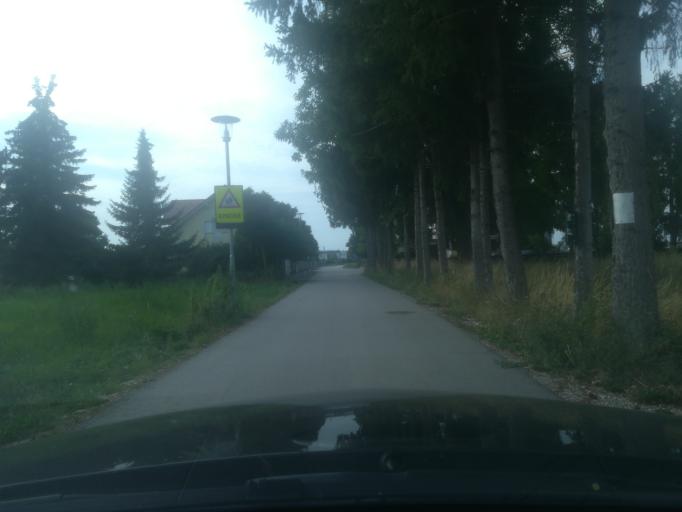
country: AT
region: Upper Austria
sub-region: Wels-Land
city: Marchtrenk
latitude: 48.1980
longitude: 14.1222
